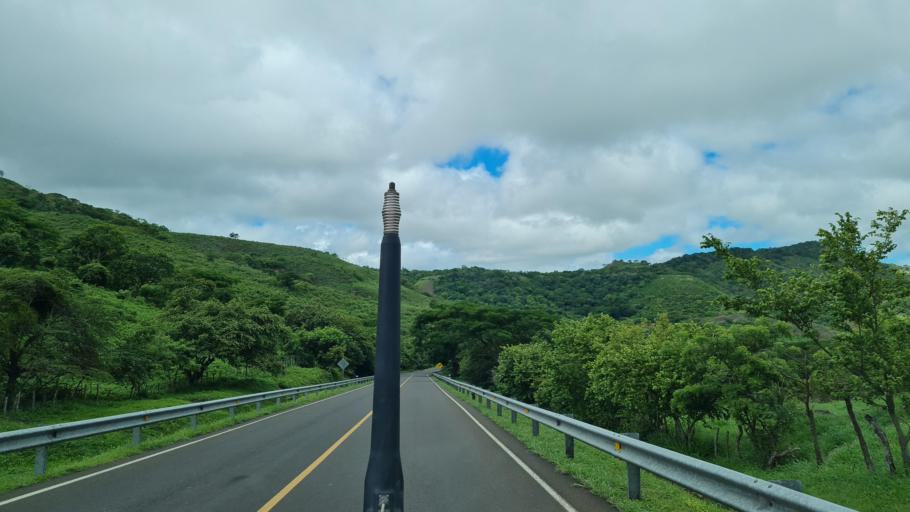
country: NI
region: Matagalpa
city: Terrabona
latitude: 12.5939
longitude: -85.9334
